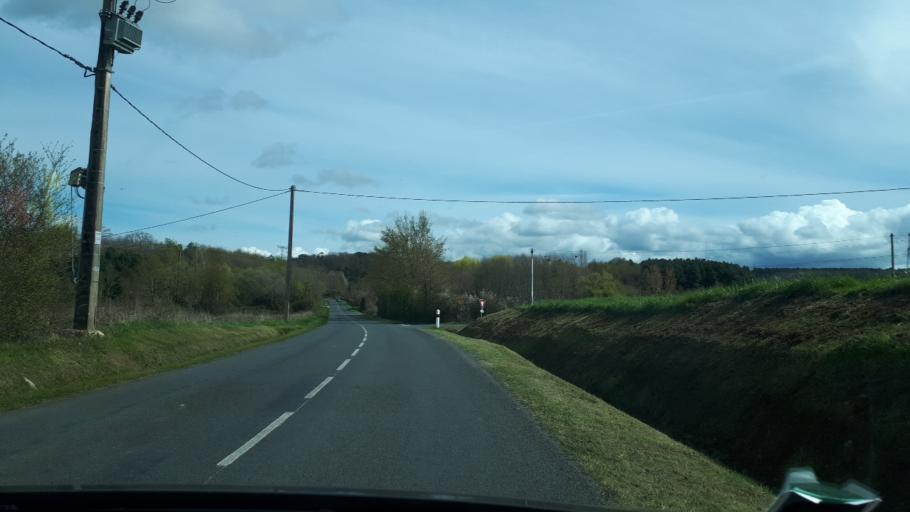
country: FR
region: Pays de la Loire
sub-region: Departement de la Sarthe
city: Ecommoy
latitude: 47.8372
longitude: 0.2826
